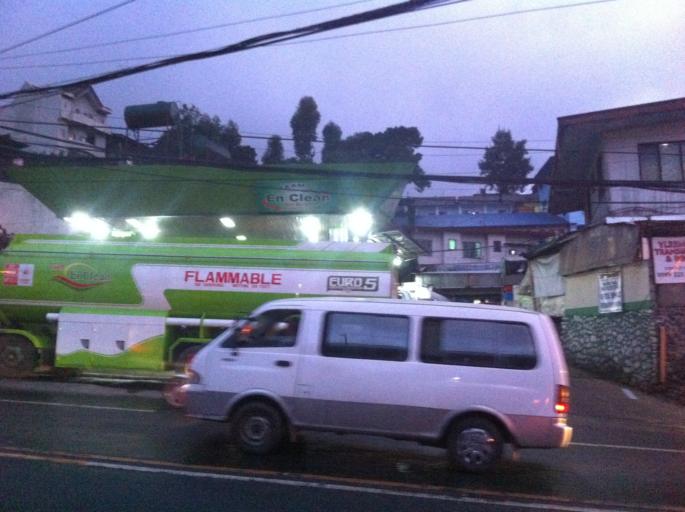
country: PH
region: Cordillera
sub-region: Baguio City
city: Baguio
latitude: 16.4206
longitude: 120.5930
